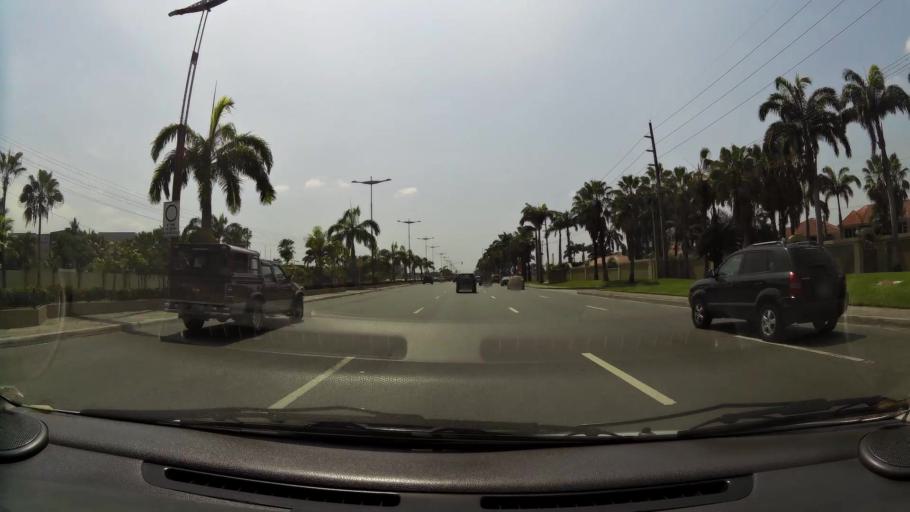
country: EC
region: Guayas
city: Eloy Alfaro
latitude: -2.1348
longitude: -79.8632
